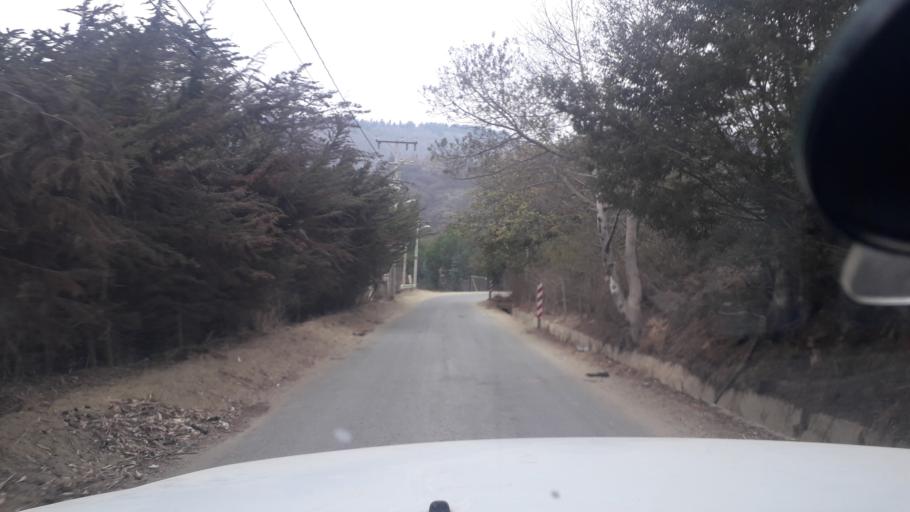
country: CL
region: Valparaiso
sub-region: Provincia de Valparaiso
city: Valparaiso
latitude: -33.1063
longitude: -71.6649
